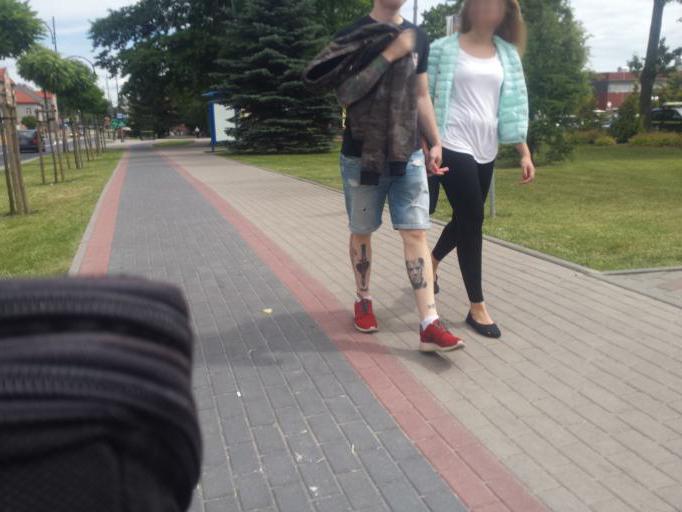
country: PL
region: Warmian-Masurian Voivodeship
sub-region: Powiat ilawski
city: Ilawa
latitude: 53.5969
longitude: 19.5631
